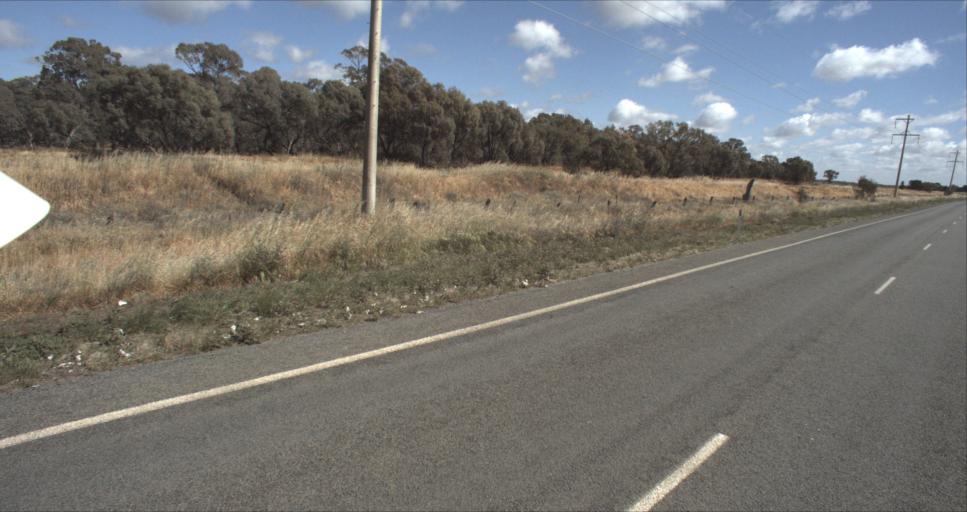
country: AU
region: New South Wales
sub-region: Murrumbidgee Shire
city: Darlington Point
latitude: -34.5453
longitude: 146.1714
